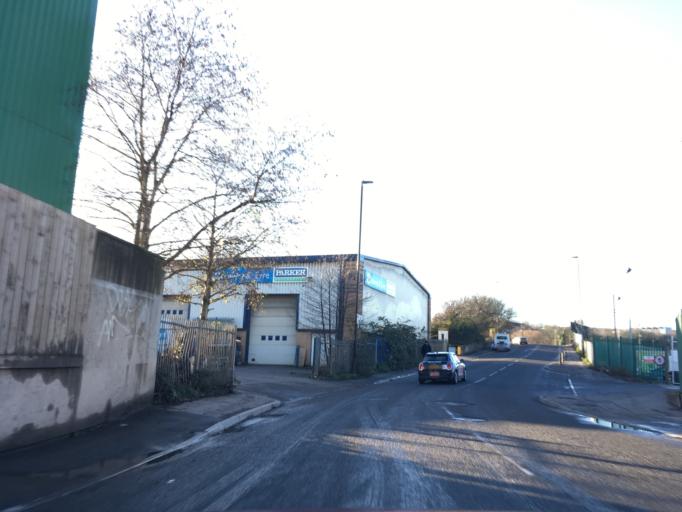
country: GB
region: England
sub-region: Bristol
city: Bristol
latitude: 51.4439
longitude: -2.5710
